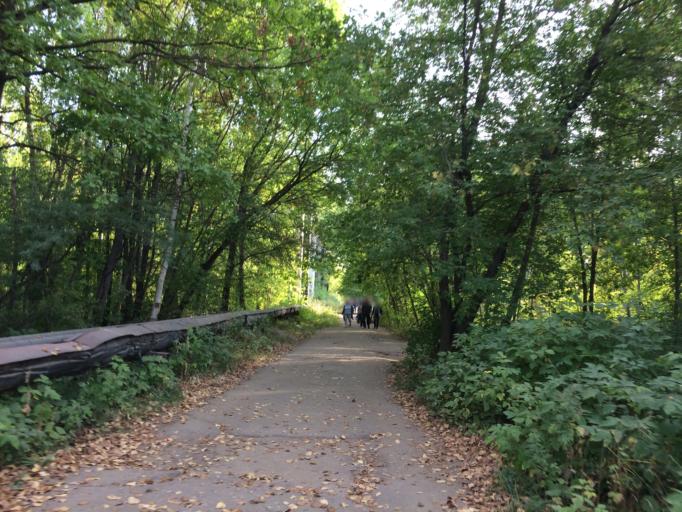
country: RU
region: Mariy-El
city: Medvedevo
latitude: 56.6268
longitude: 47.8192
